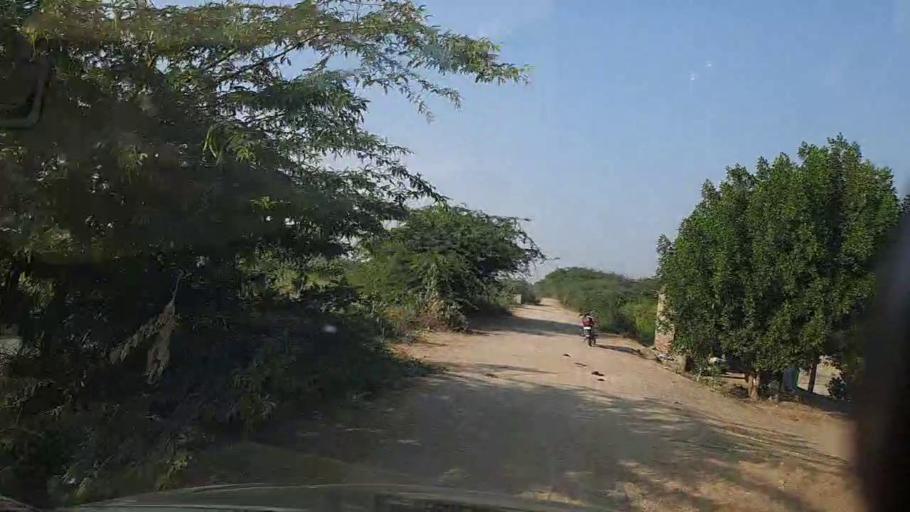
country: PK
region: Sindh
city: Thatta
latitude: 24.6171
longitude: 67.8762
